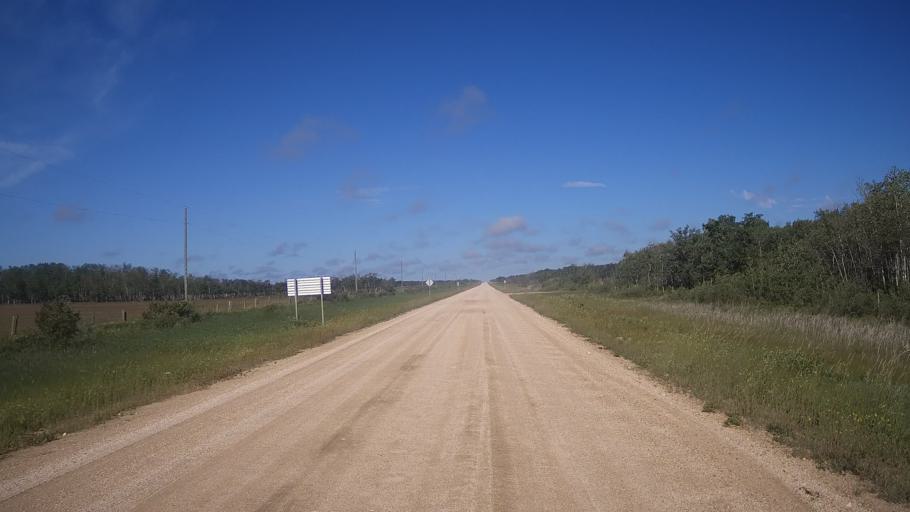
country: CA
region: Manitoba
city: Stonewall
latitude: 50.2411
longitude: -97.7168
